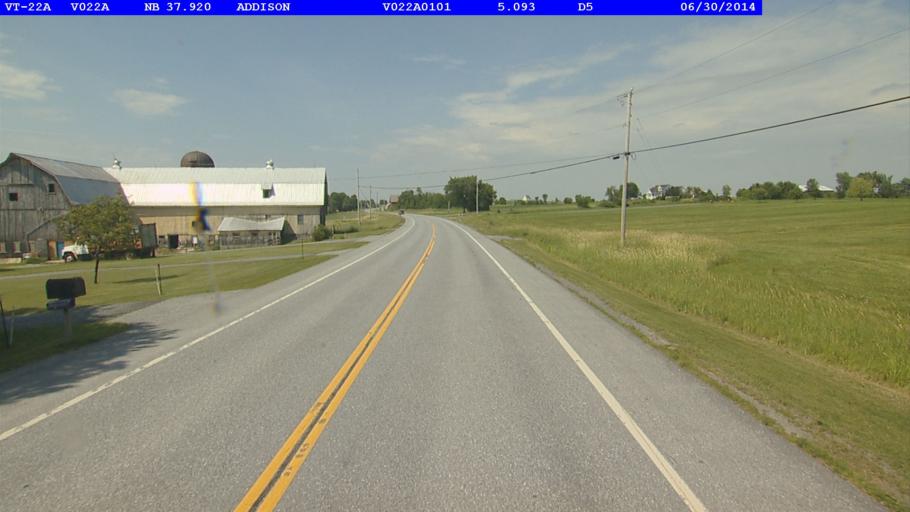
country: US
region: Vermont
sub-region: Addison County
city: Vergennes
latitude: 44.1021
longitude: -73.2963
